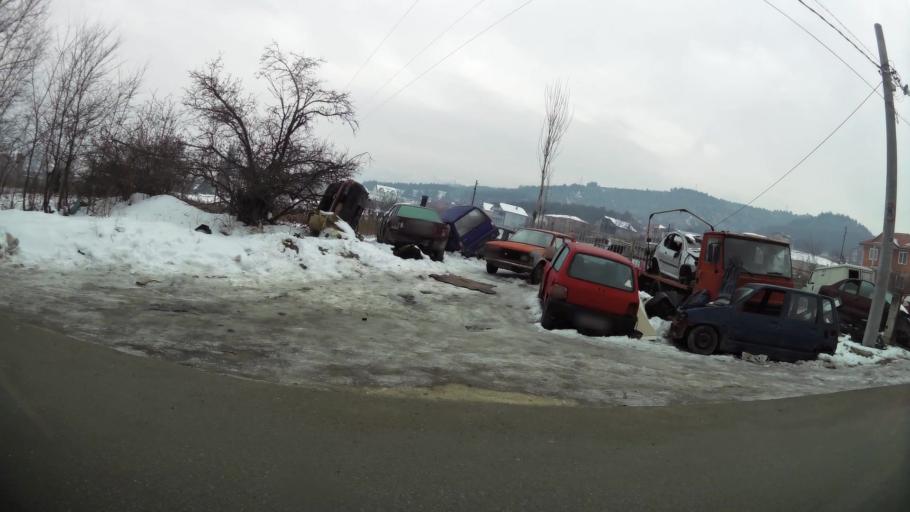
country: MK
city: Kondovo
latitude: 42.0127
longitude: 21.3056
